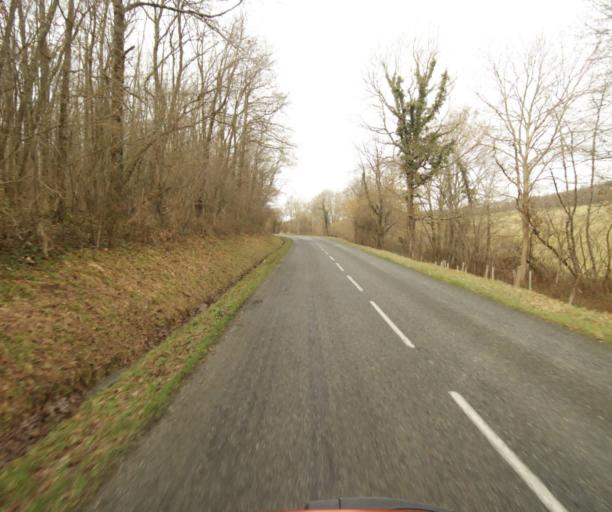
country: FR
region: Midi-Pyrenees
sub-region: Departement de l'Ariege
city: Pamiers
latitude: 43.1465
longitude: 1.5257
